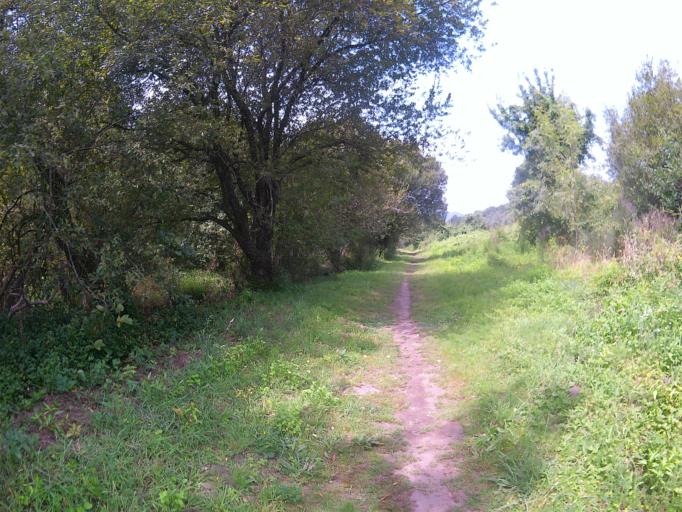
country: PT
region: Viana do Castelo
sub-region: Ponte de Lima
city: Ponte de Lima
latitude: 41.7788
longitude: -8.5755
